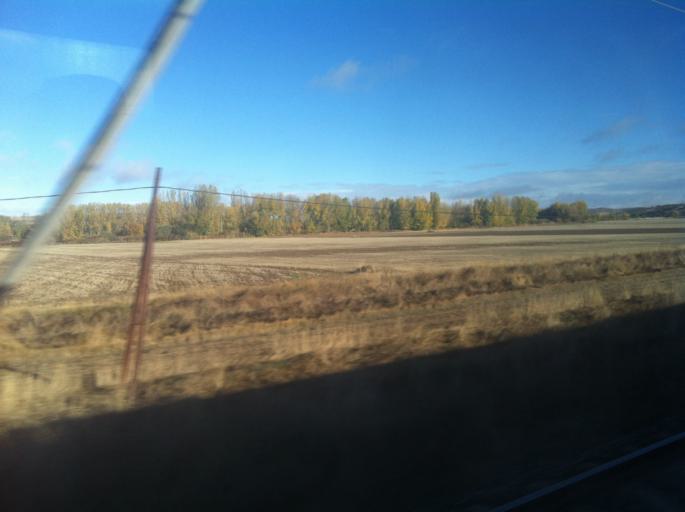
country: ES
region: Castille and Leon
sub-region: Provincia de Burgos
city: Celada del Camino
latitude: 42.2599
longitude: -3.9260
